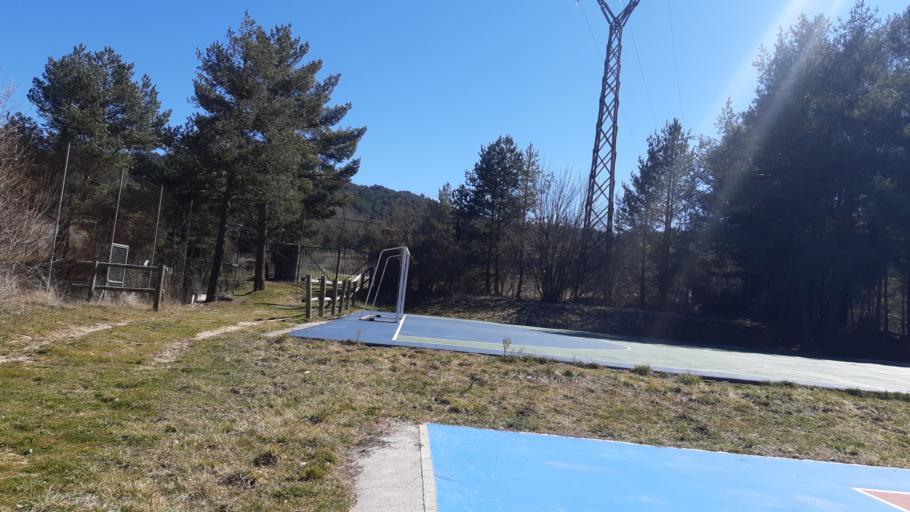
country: ES
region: Madrid
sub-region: Provincia de Madrid
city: Guadarrama
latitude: 40.7179
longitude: -4.1611
